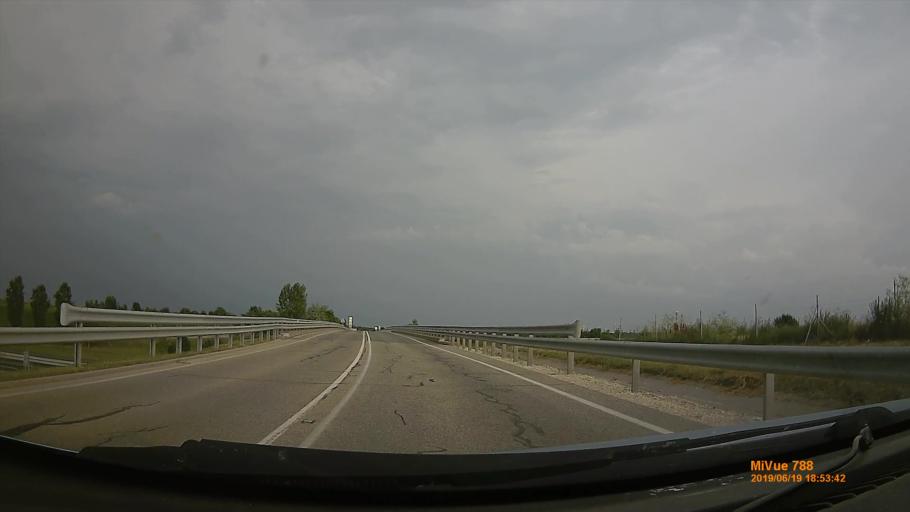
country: HU
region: Fejer
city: Rackeresztur
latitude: 47.3056
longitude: 18.8662
